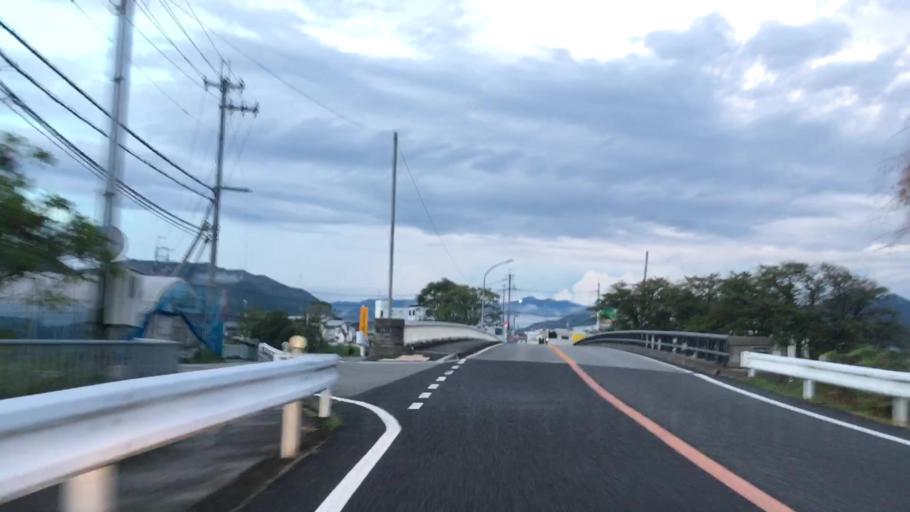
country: JP
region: Hyogo
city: Himeji
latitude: 34.9471
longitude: 134.7480
